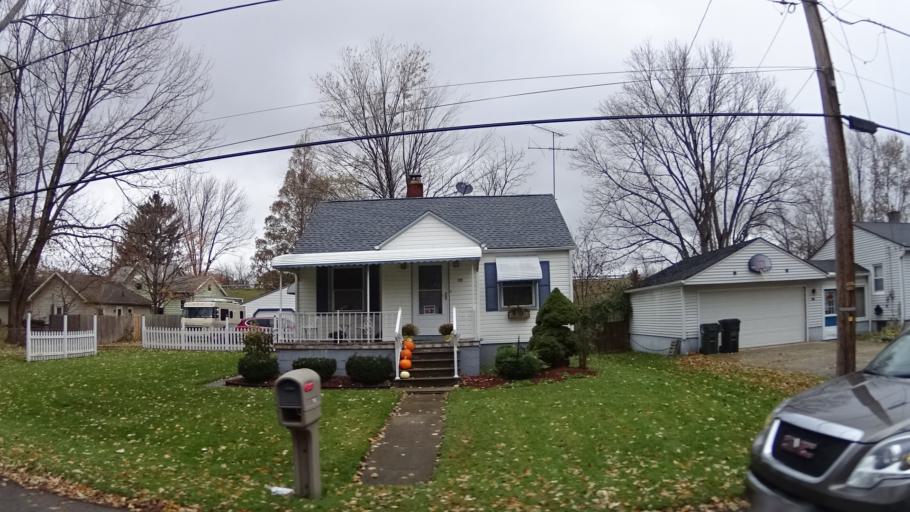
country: US
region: Ohio
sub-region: Lorain County
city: Elyria
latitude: 41.3904
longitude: -82.1294
